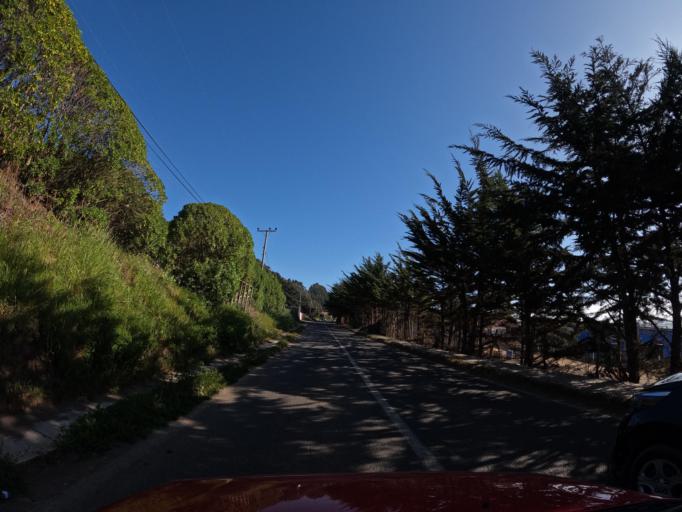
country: CL
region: Maule
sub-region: Provincia de Talca
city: Constitucion
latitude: -34.8708
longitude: -72.1510
